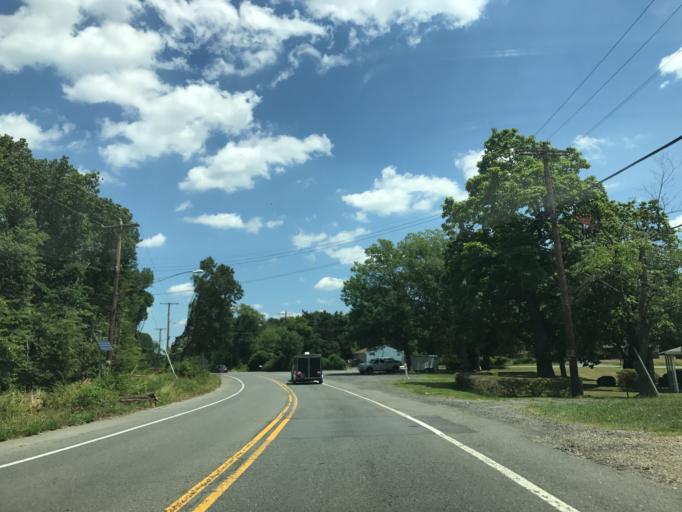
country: US
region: Maryland
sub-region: Prince George's County
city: South Laurel
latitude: 39.0564
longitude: -76.8709
